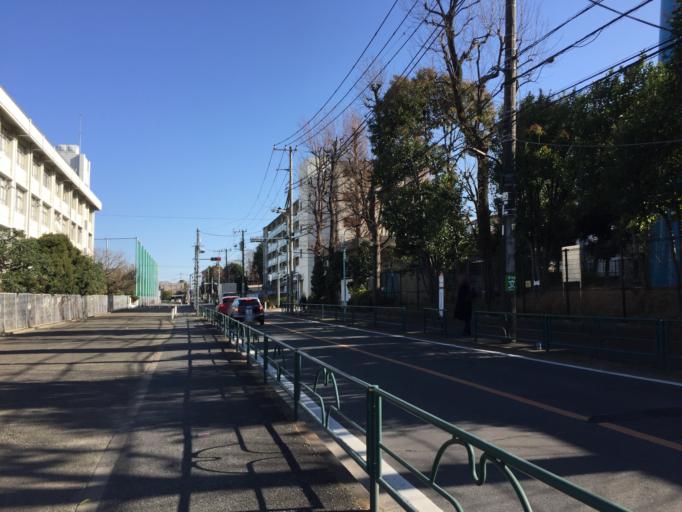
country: JP
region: Tokyo
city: Chofugaoka
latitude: 35.6256
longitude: 139.5932
